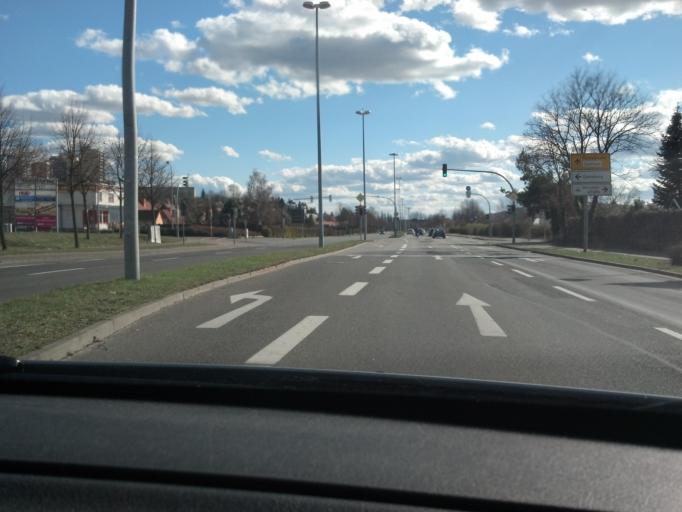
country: DE
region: Mecklenburg-Vorpommern
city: Neubrandenburg
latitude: 53.5809
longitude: 13.2707
